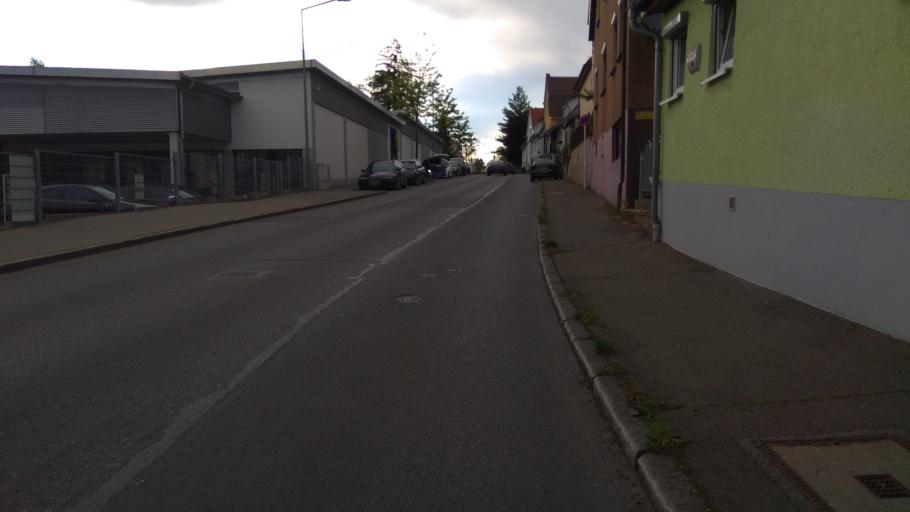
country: DE
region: Baden-Wuerttemberg
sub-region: Tuebingen Region
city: Wannweil
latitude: 48.5007
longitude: 9.1749
